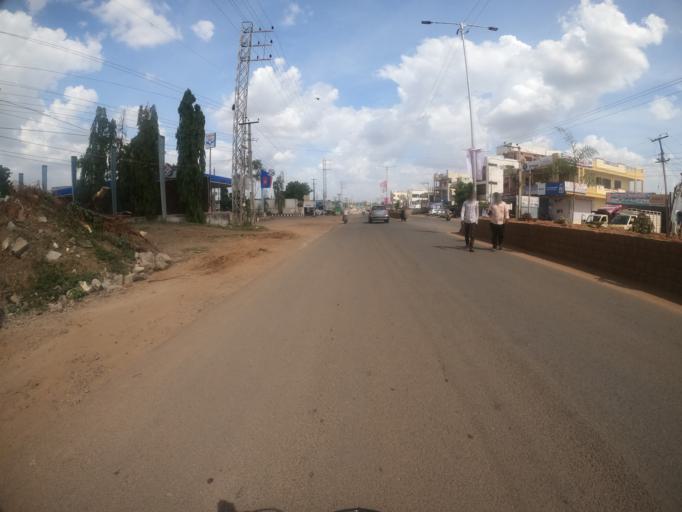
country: IN
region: Telangana
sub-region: Rangareddi
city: Sriramnagar
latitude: 17.3096
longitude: 78.1423
